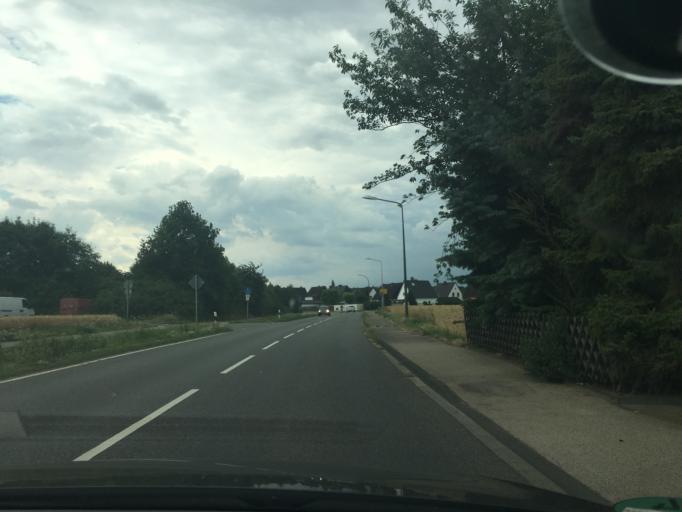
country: DE
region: North Rhine-Westphalia
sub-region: Regierungsbezirk Koln
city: Dueren
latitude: 50.8225
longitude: 6.4907
